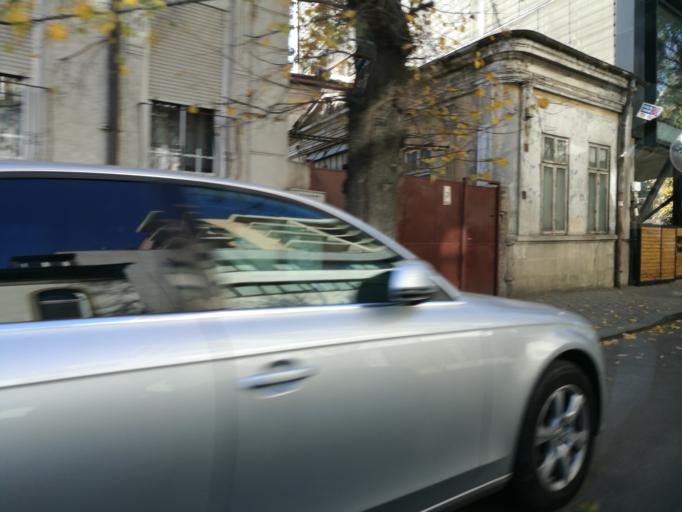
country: RO
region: Bucuresti
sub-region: Municipiul Bucuresti
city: Bucharest
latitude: 44.4450
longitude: 26.1172
